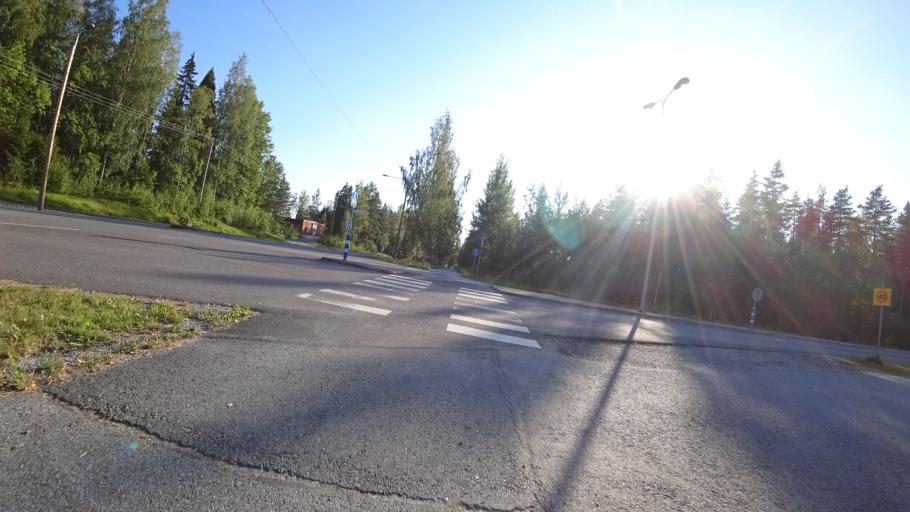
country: FI
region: Pirkanmaa
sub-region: Tampere
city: Nokia
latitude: 61.4695
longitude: 23.4545
